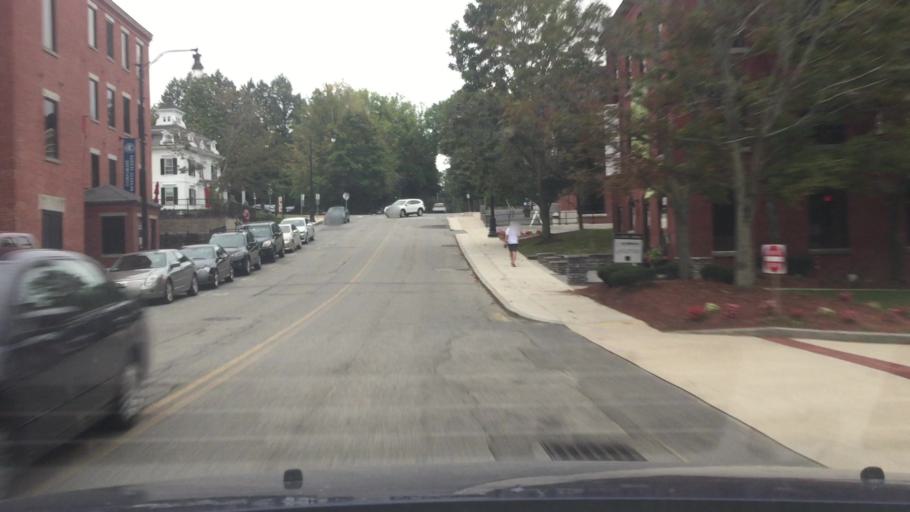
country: US
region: Massachusetts
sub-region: Essex County
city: North Andover
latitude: 42.7015
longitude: -71.1254
